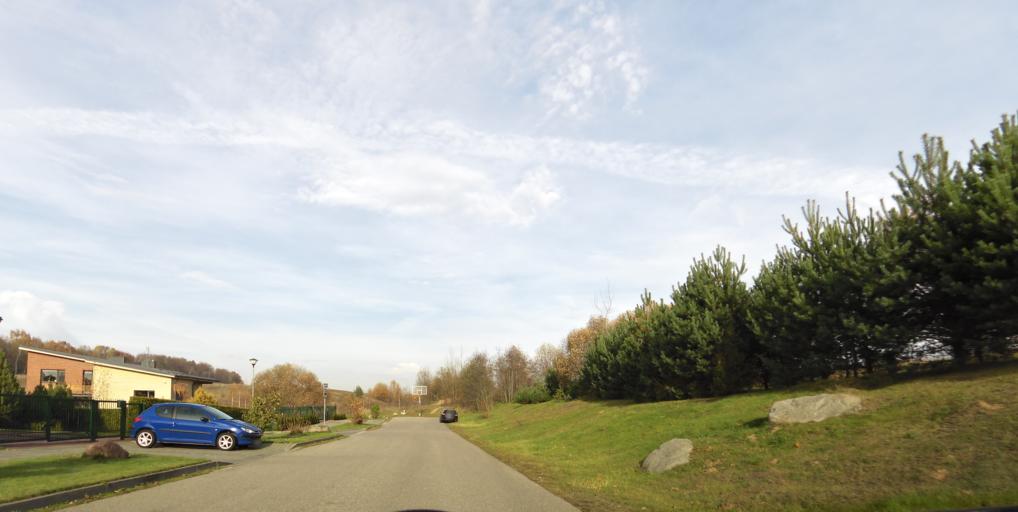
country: LT
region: Vilnius County
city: Justiniskes
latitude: 54.7137
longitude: 25.2060
